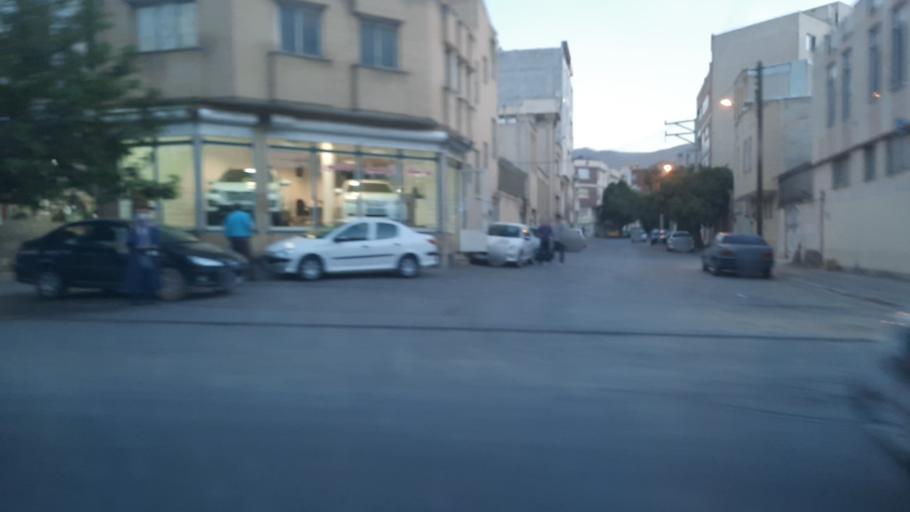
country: IR
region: Markazi
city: Arak
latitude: 34.0755
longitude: 49.7002
